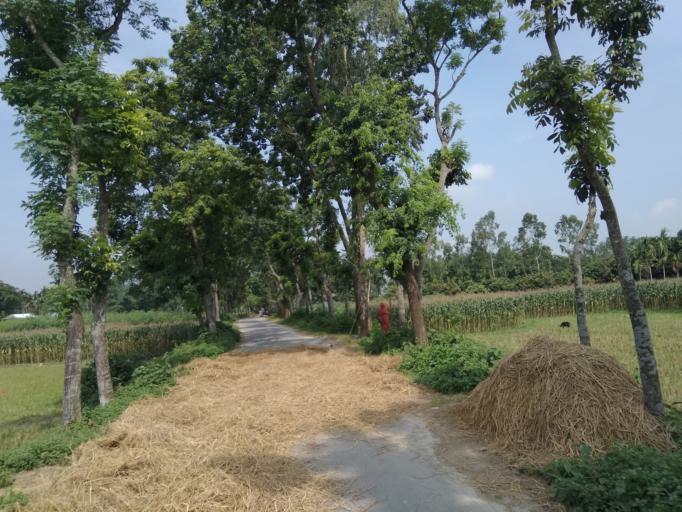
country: BD
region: Rangpur Division
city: Rangpur
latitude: 25.8362
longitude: 89.1981
